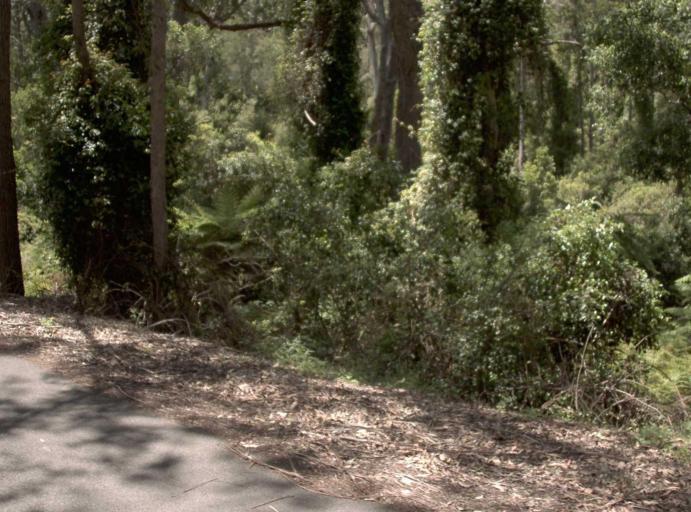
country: AU
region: New South Wales
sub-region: Bombala
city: Bombala
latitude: -37.4781
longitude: 148.9267
